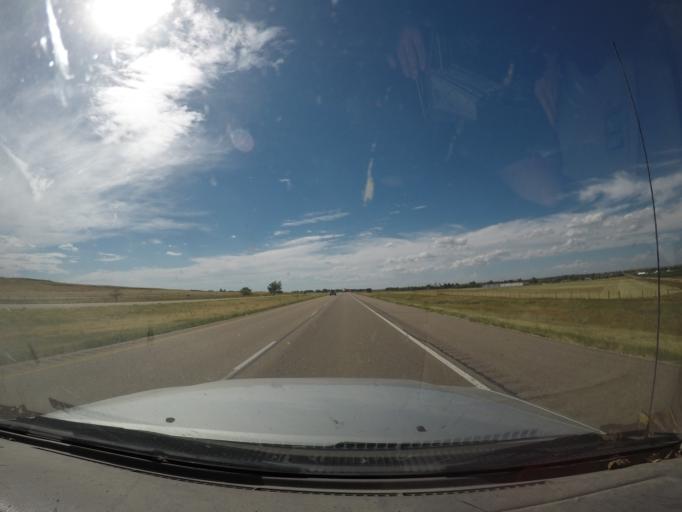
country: US
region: Nebraska
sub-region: Deuel County
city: Chappell
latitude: 41.0717
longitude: -102.4574
